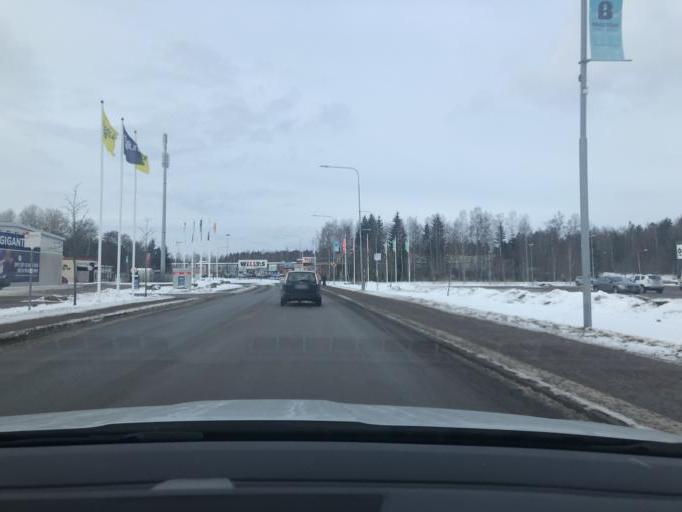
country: SE
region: OEstergoetland
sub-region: Motala Kommun
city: Motala
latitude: 58.5571
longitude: 15.0395
